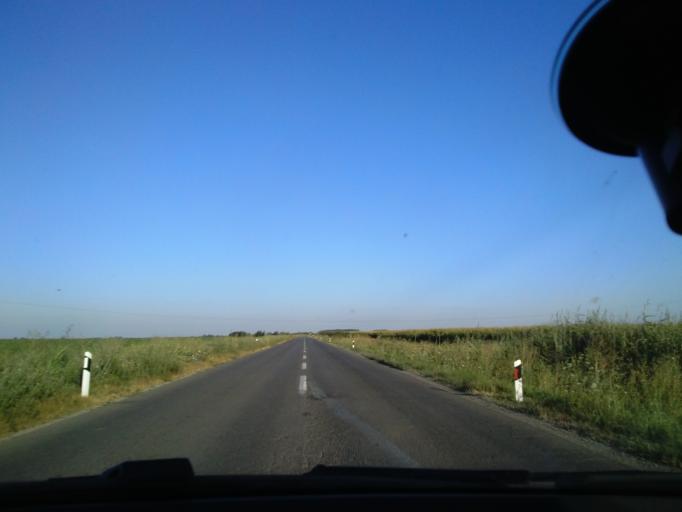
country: RS
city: Maglic
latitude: 45.3822
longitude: 19.5117
